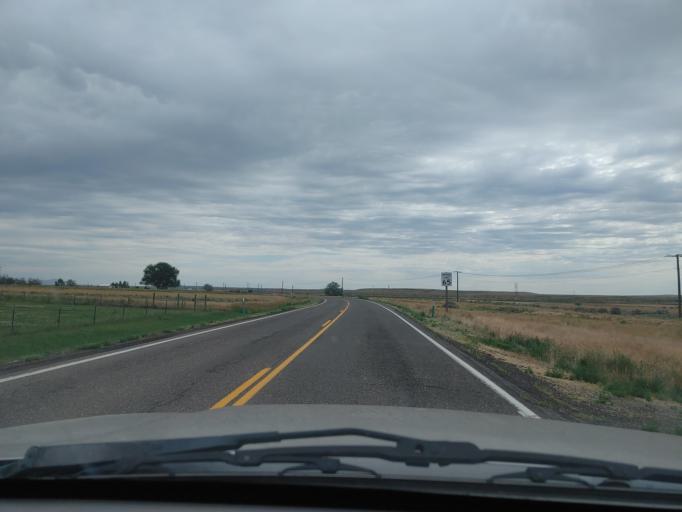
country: US
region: Idaho
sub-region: Lincoln County
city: Shoshone
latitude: 43.0495
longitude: -114.1449
